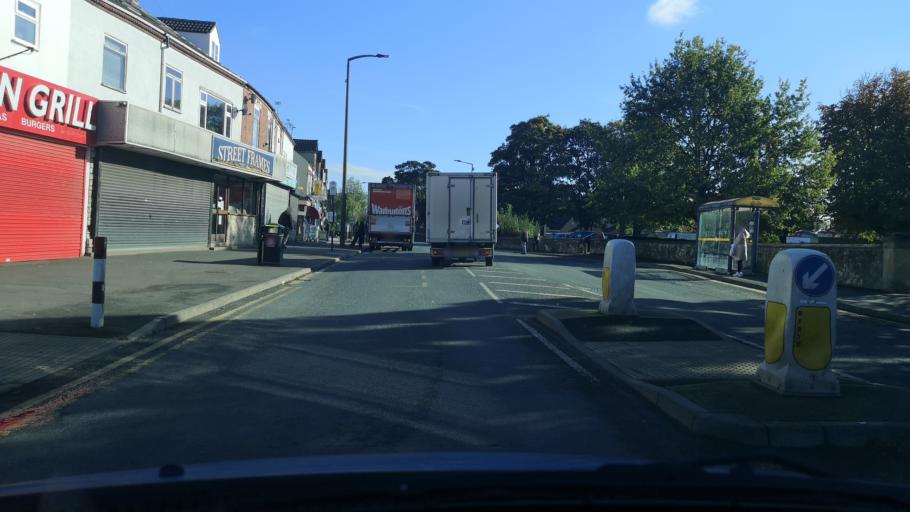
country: GB
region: England
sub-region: Doncaster
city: Askern
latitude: 53.6160
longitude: -1.1515
